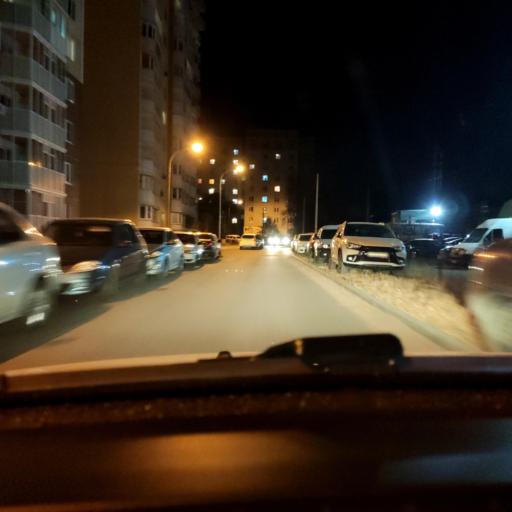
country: RU
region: Voronezj
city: Podgornoye
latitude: 51.7300
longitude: 39.2015
